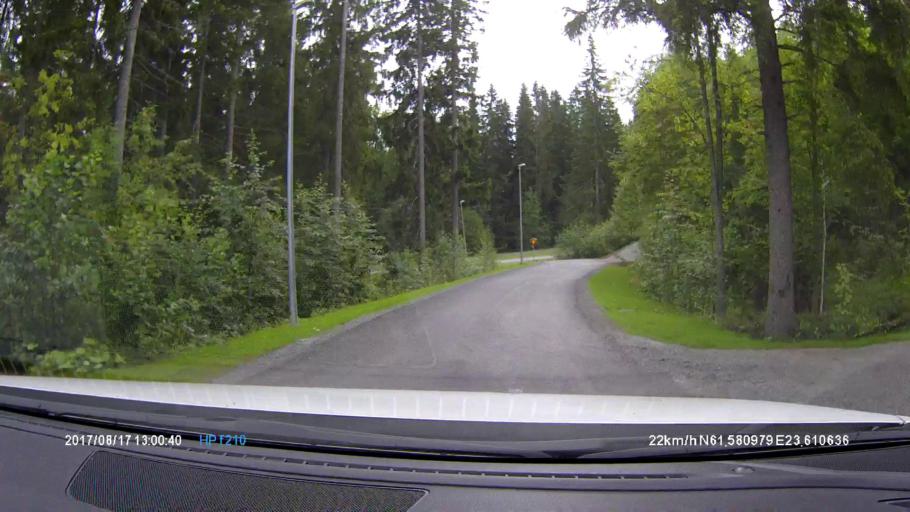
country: FI
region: Pirkanmaa
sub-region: Tampere
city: Yloejaervi
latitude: 61.5808
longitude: 23.6108
